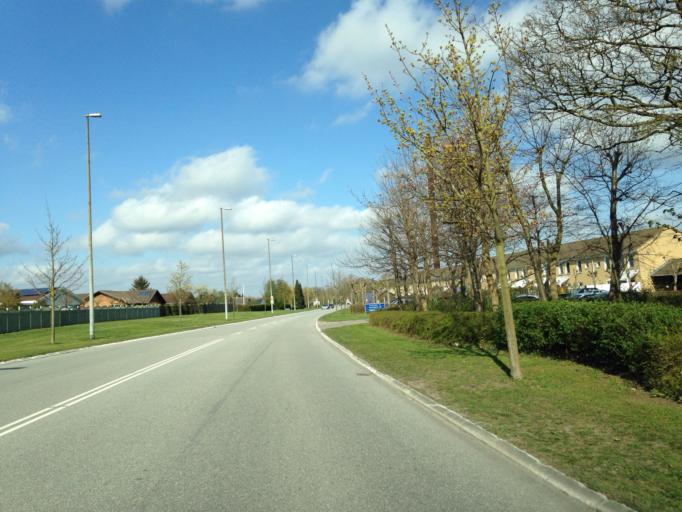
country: DK
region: Zealand
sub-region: Greve Kommune
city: Greve
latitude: 55.5869
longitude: 12.2715
